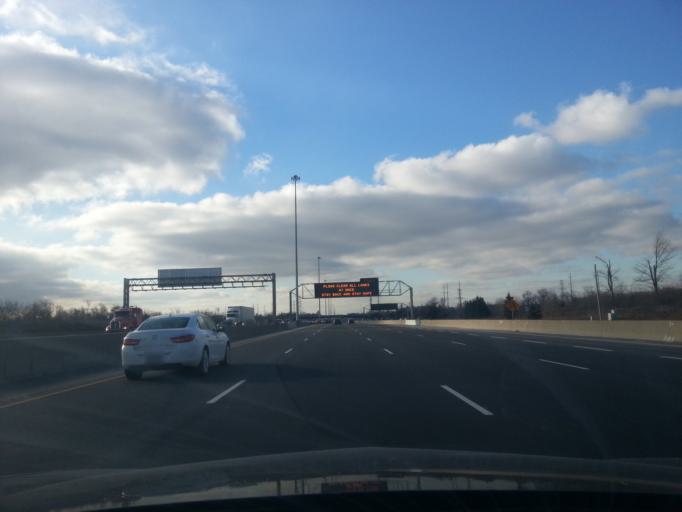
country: CA
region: Ontario
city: Scarborough
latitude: 43.7993
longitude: -79.1785
